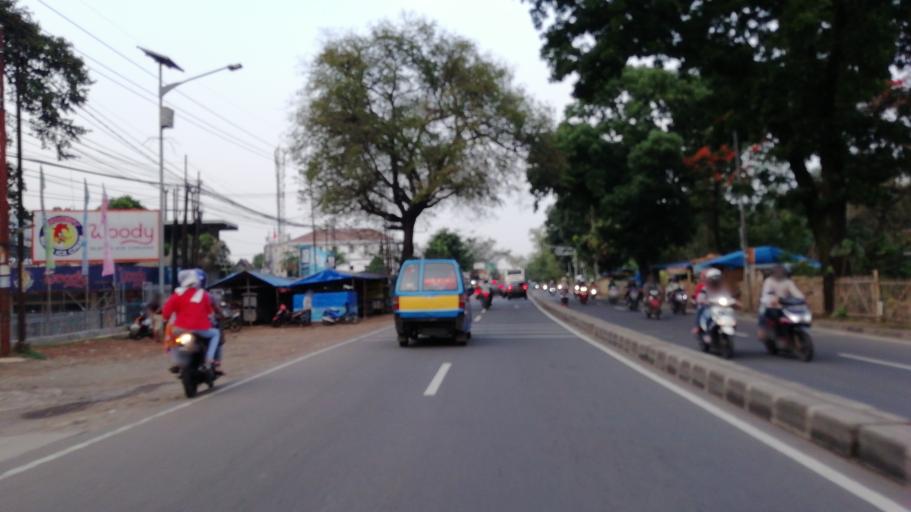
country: ID
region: West Java
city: Depok
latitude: -6.4126
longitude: 106.8605
